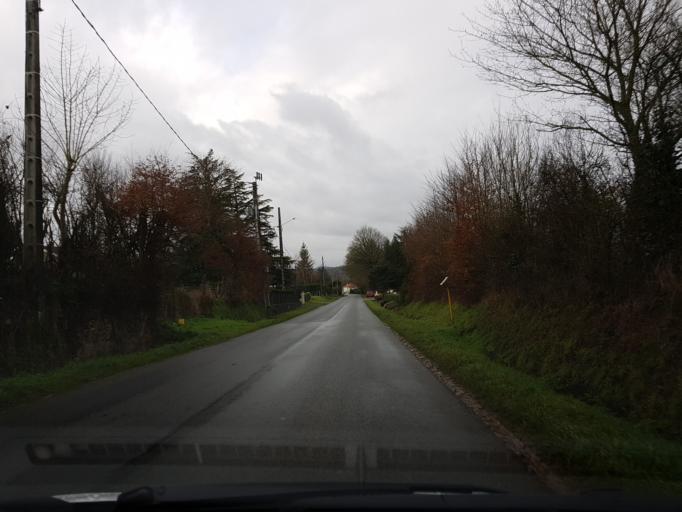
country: FR
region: Poitou-Charentes
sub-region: Departement de la Charente
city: Chabanais
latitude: 45.8856
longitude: 0.7242
